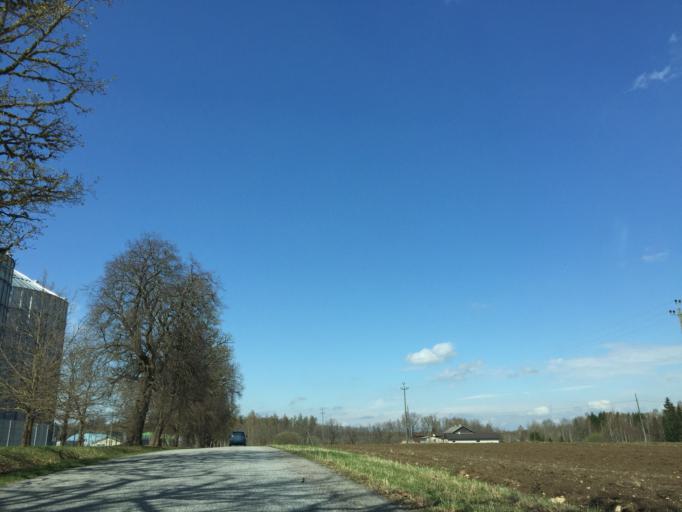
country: EE
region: Tartu
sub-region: Elva linn
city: Elva
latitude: 58.1480
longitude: 26.2334
